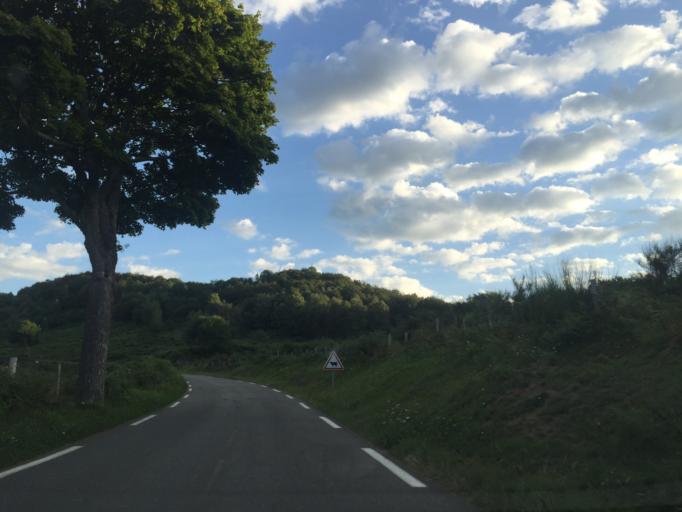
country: FR
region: Midi-Pyrenees
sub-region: Departement des Hautes-Pyrenees
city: Saint-Lary-Soulan
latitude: 42.9272
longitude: 0.3513
